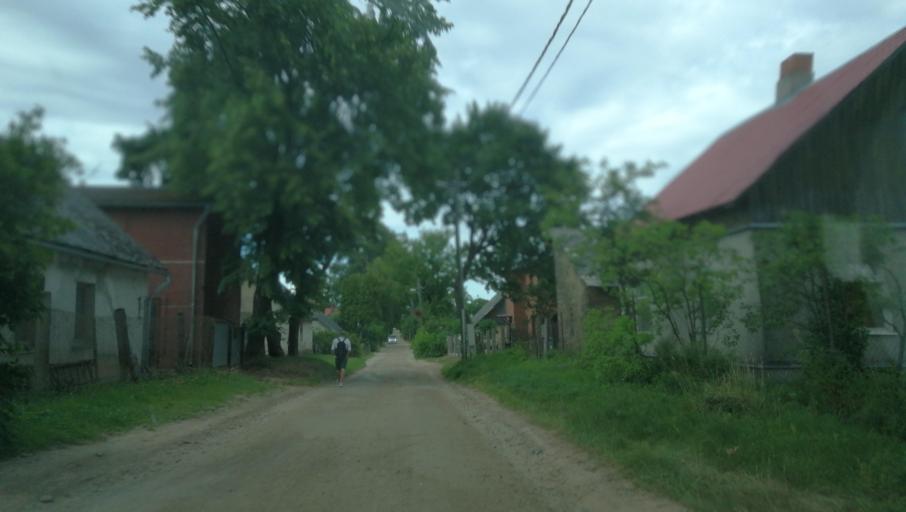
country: LV
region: Cesu Rajons
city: Cesis
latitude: 57.3103
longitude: 25.2935
